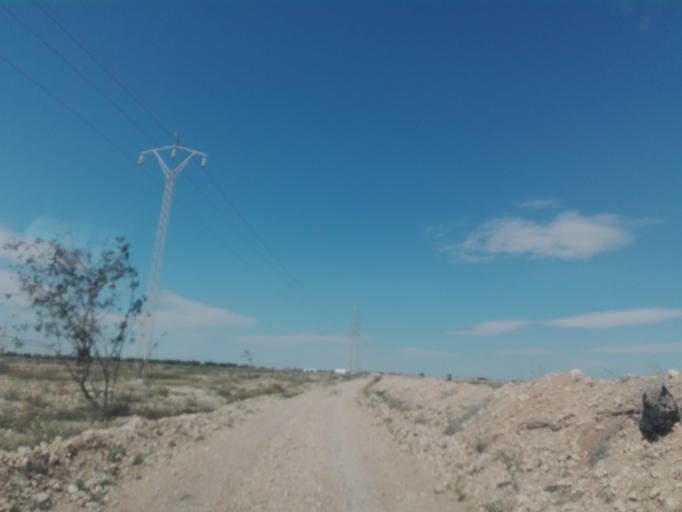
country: TN
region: Safaqis
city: Sfax
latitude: 34.6879
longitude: 10.5381
